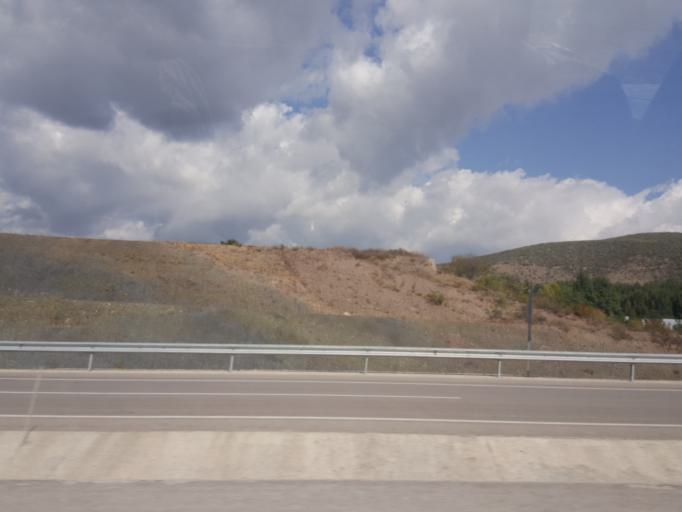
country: TR
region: Tokat
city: Gokdere
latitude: 40.3794
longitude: 36.6808
